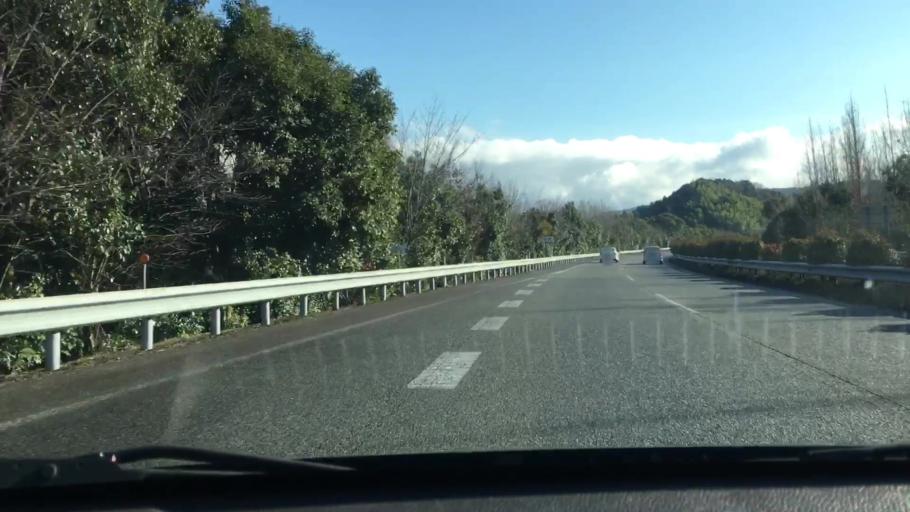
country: JP
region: Kumamoto
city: Hitoyoshi
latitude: 32.1975
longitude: 130.7773
